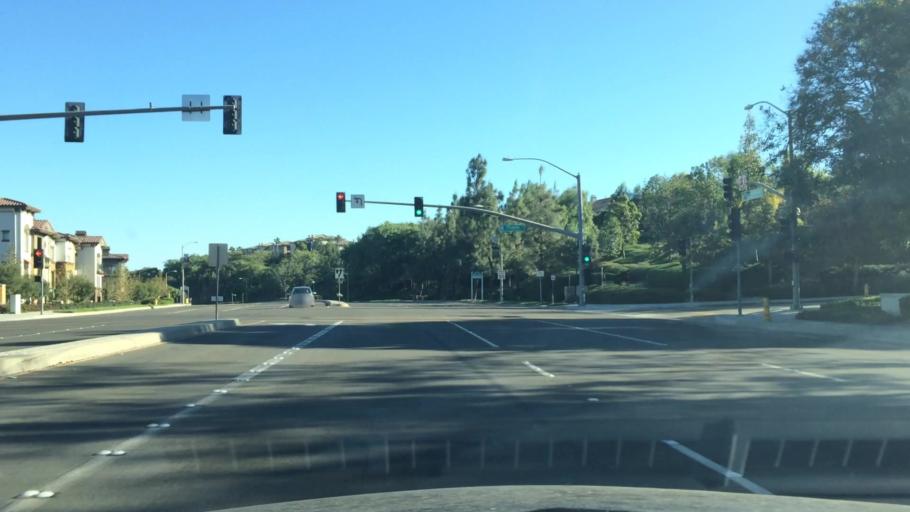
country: US
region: California
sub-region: San Bernardino County
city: Los Serranos
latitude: 33.9577
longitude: -117.6900
